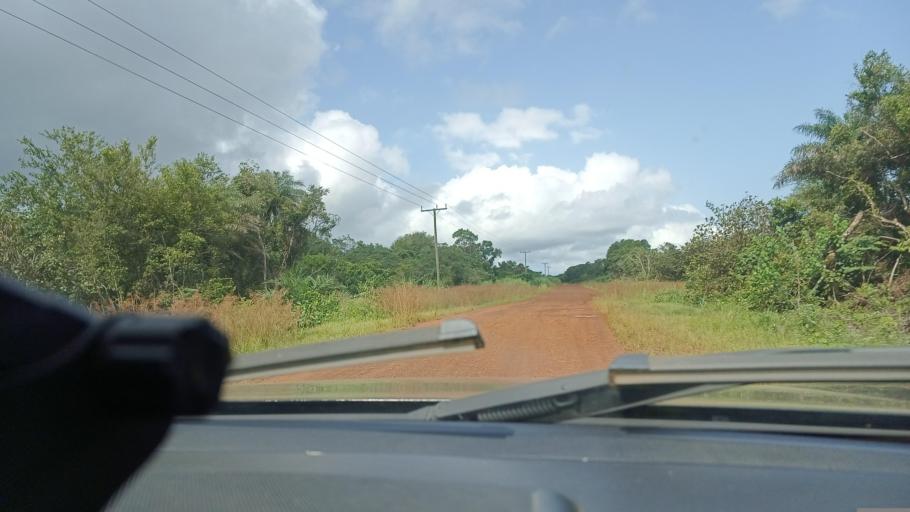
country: LR
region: Grand Cape Mount
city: Robertsport
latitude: 6.6897
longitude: -11.2590
